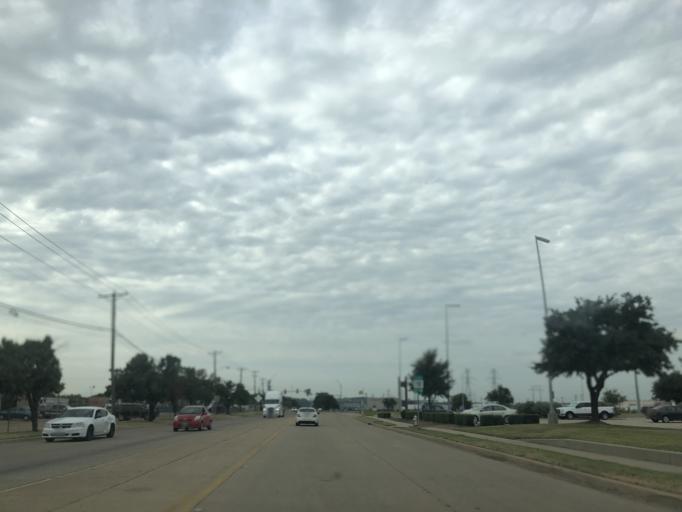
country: US
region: Texas
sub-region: Tarrant County
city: Richland Hills
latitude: 32.7998
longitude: -97.2212
